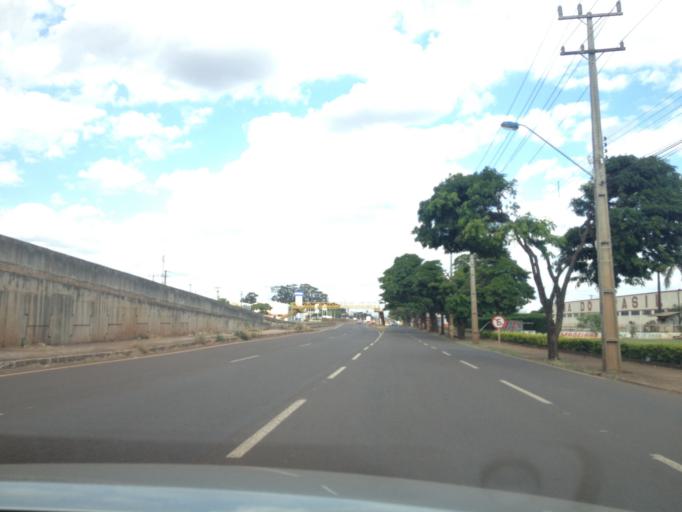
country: BR
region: Parana
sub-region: Sarandi
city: Sarandi
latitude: -23.4329
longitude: -51.8861
